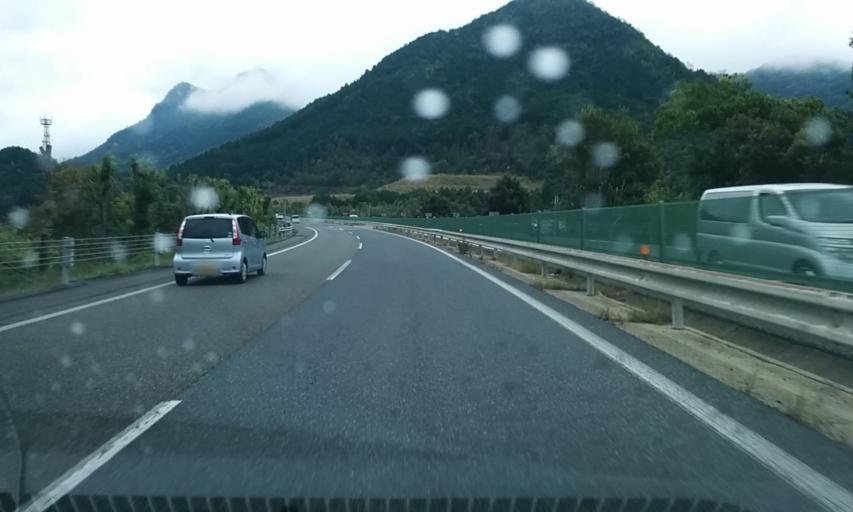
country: JP
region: Hyogo
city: Sasayama
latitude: 35.1420
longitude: 135.1289
